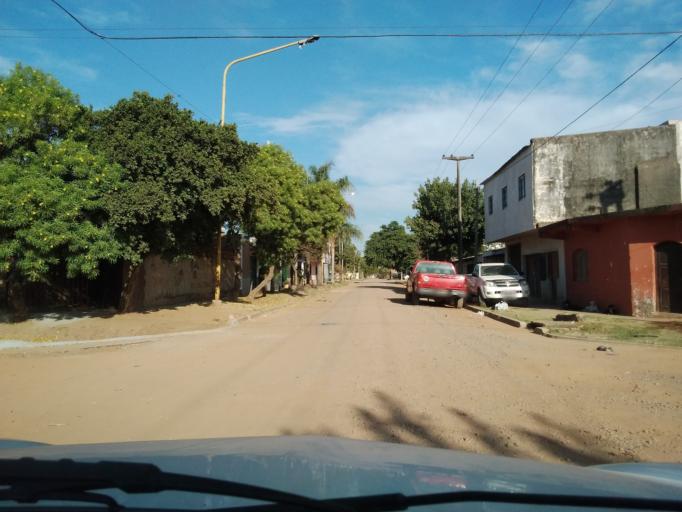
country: AR
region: Corrientes
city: Corrientes
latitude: -27.4919
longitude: -58.7841
